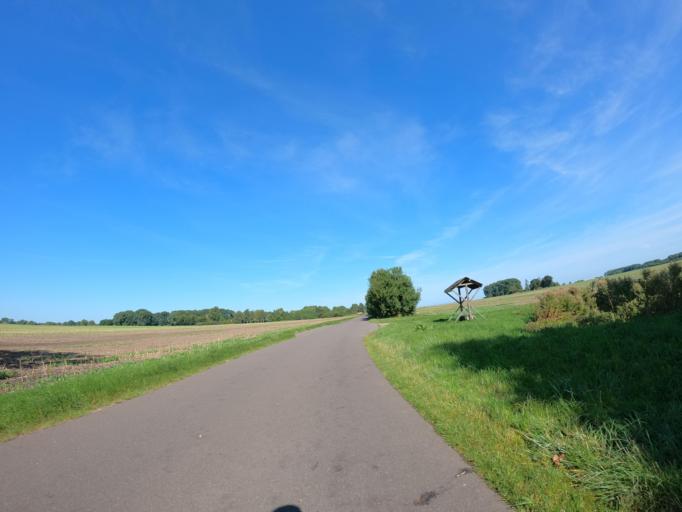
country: DE
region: Mecklenburg-Vorpommern
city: Kramerhof
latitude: 54.3651
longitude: 13.0500
